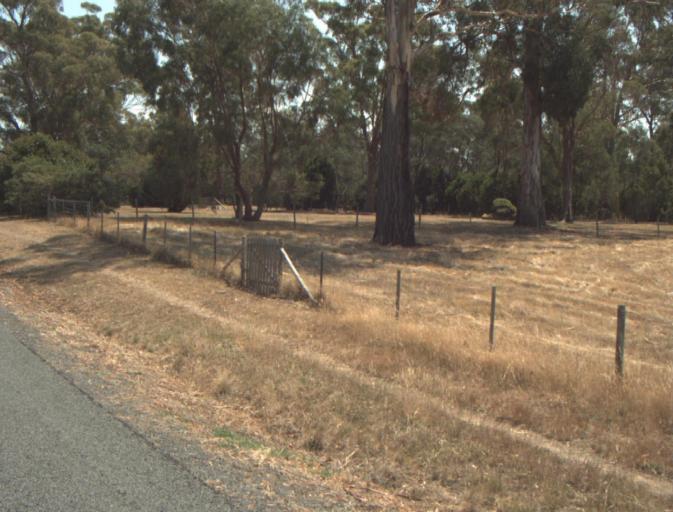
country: AU
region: Tasmania
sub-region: Launceston
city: Newstead
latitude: -41.5003
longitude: 147.2097
